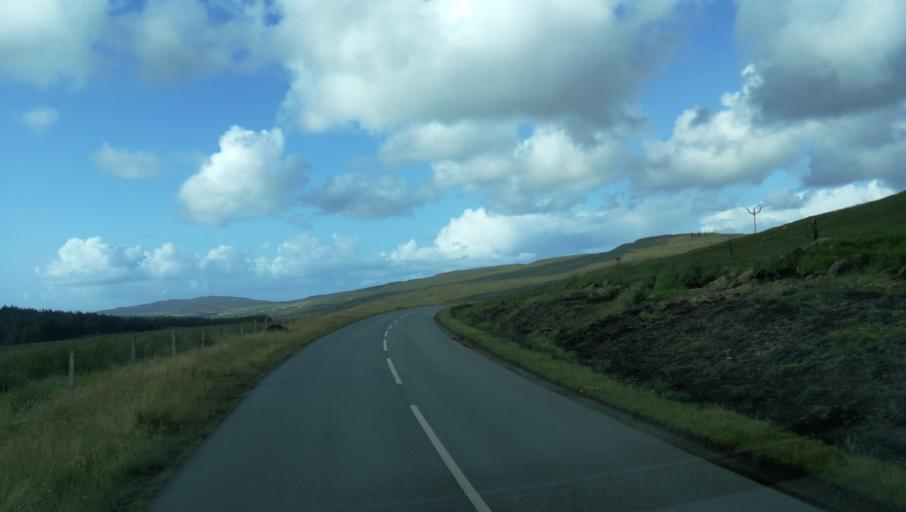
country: GB
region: Scotland
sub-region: Highland
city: Isle of Skye
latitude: 57.4624
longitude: -6.5425
